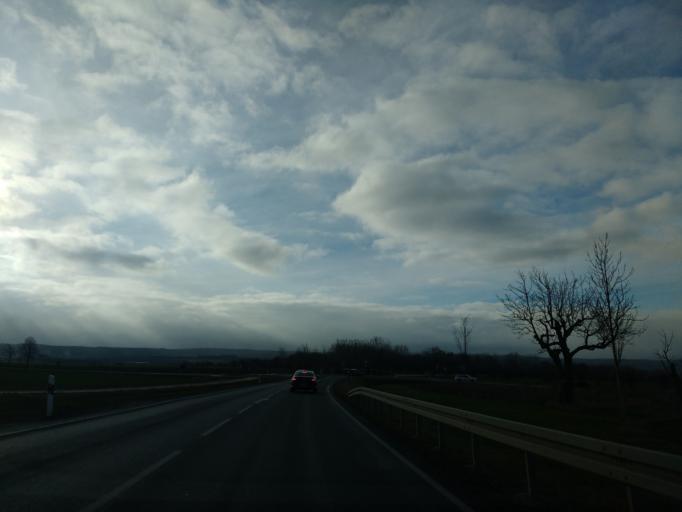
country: DE
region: Saxony-Anhalt
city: Quedlinburg
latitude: 51.7597
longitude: 11.1535
